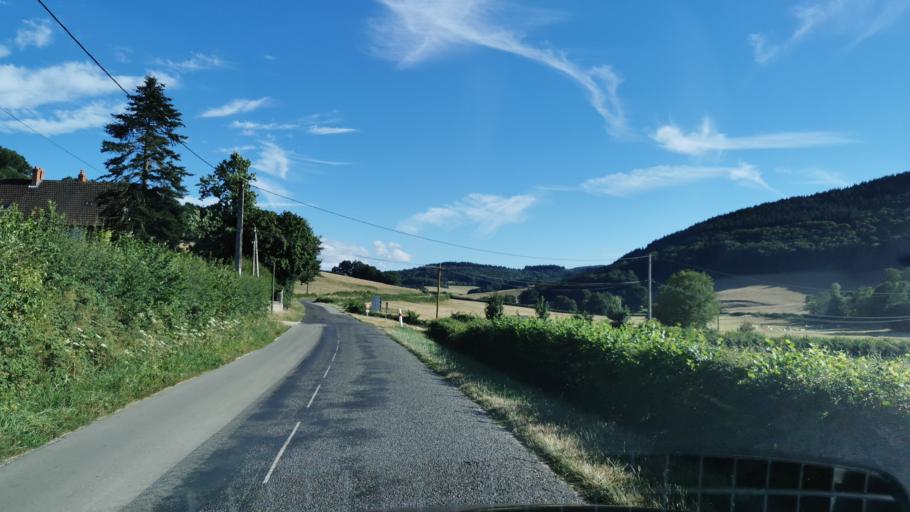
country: FR
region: Bourgogne
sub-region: Departement de Saone-et-Loire
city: Marmagne
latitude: 46.8389
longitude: 4.3188
